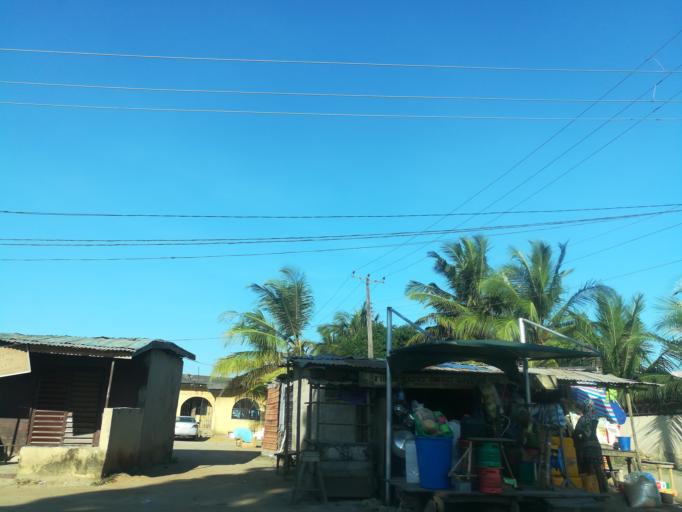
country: NG
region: Lagos
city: Ebute Ikorodu
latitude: 6.5535
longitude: 3.5393
